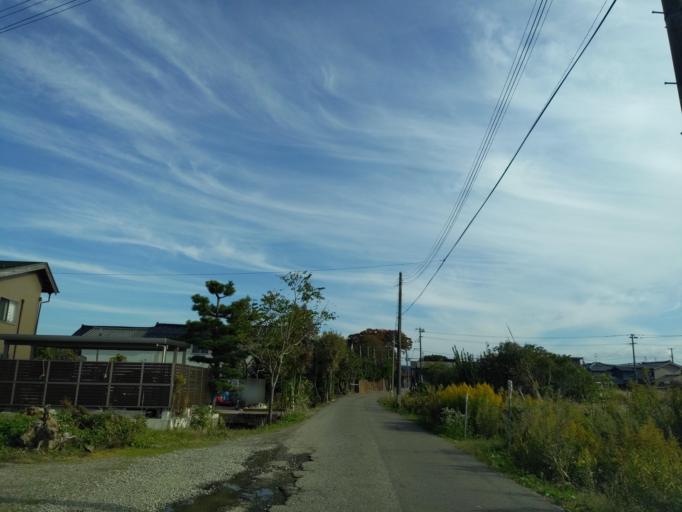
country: JP
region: Niigata
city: Sanjo
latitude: 37.6141
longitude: 138.9464
